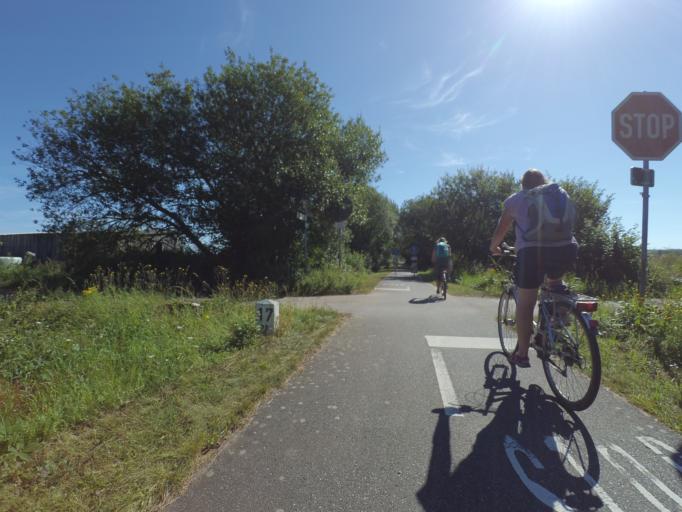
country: DE
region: Rheinland-Pfalz
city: Niederofflingen
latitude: 50.0712
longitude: 6.8850
